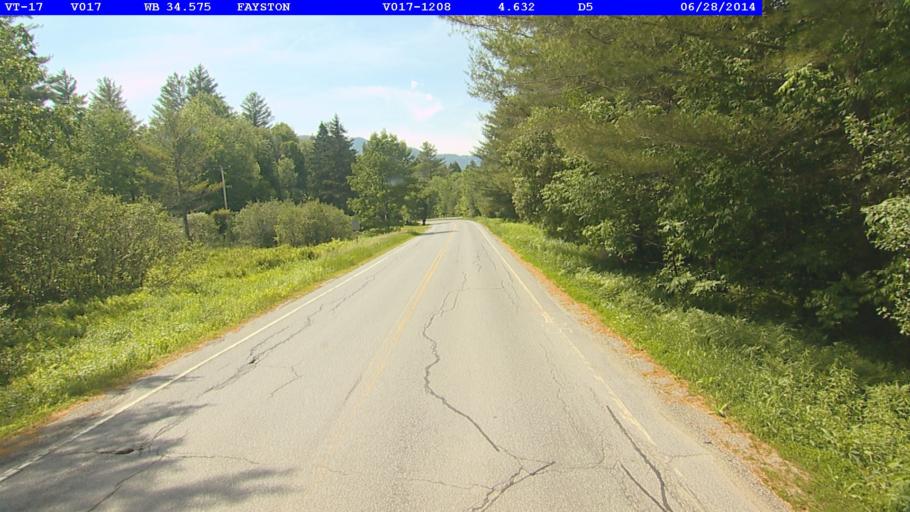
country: US
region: Vermont
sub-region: Washington County
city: Waterbury
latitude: 44.1826
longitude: -72.8662
